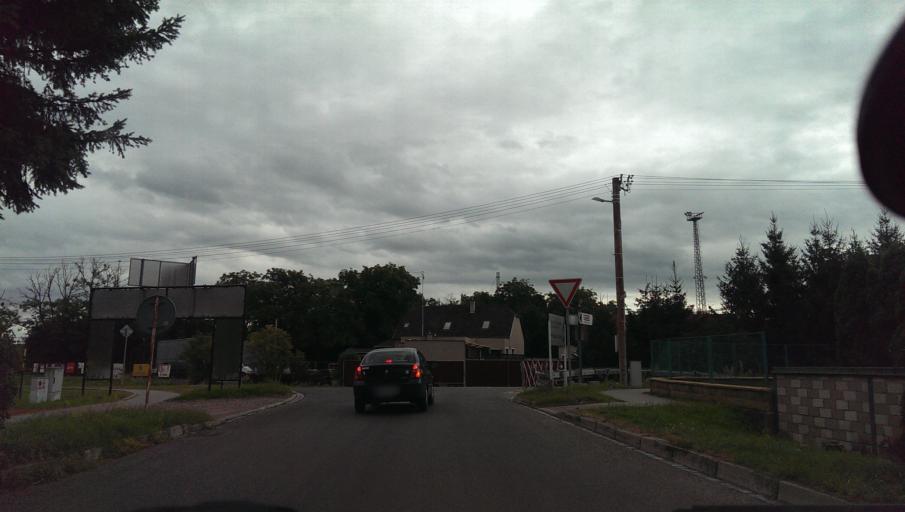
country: CZ
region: South Moravian
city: Moravsky Pisek
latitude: 48.9800
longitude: 17.3156
